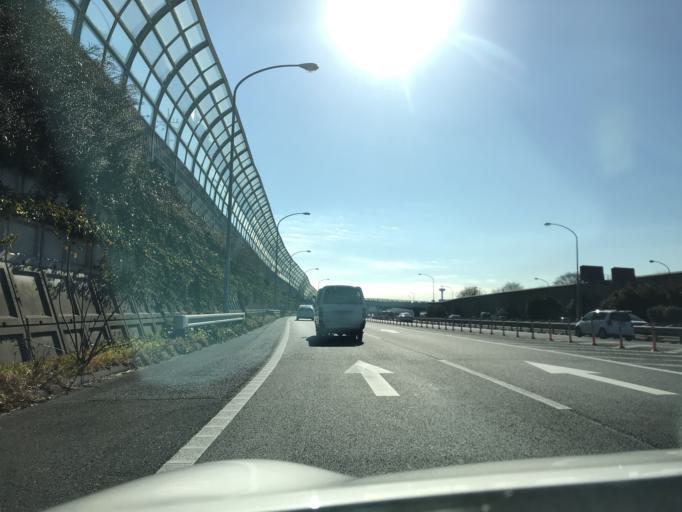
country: JP
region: Chiba
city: Chiba
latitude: 35.6599
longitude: 140.1020
